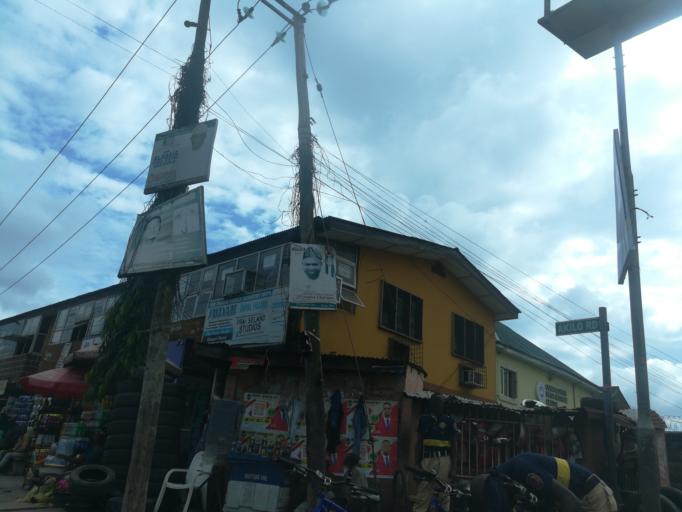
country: NG
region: Lagos
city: Agege
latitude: 6.6257
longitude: 3.3346
